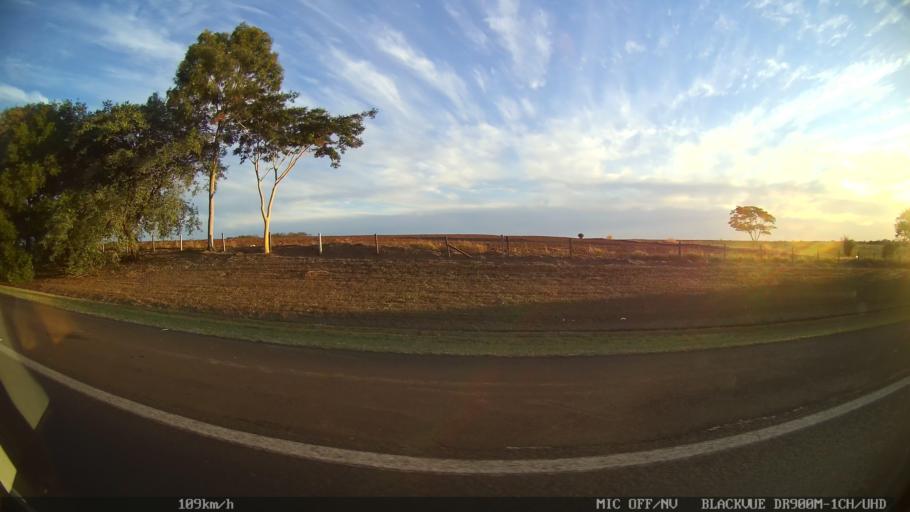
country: BR
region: Sao Paulo
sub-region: Catanduva
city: Catanduva
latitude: -21.1708
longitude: -48.9727
